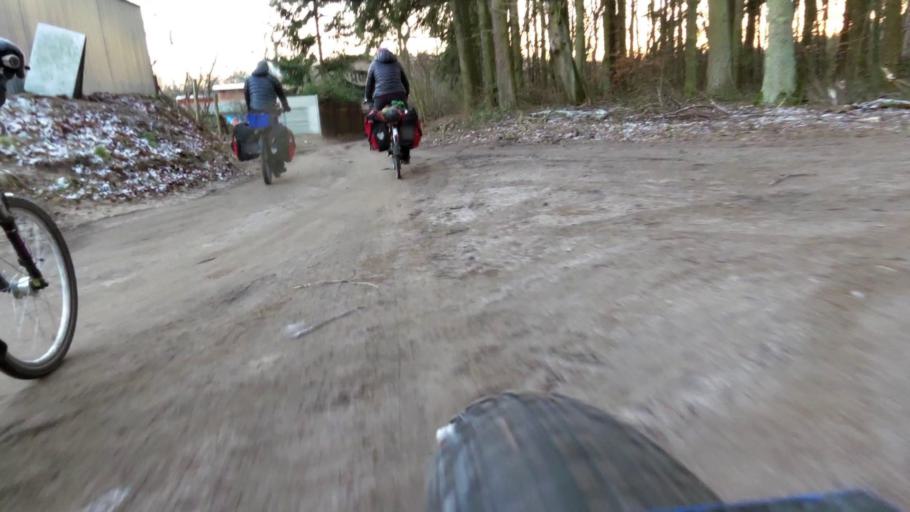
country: PL
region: West Pomeranian Voivodeship
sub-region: Powiat walecki
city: Walcz
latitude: 53.2512
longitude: 16.3727
